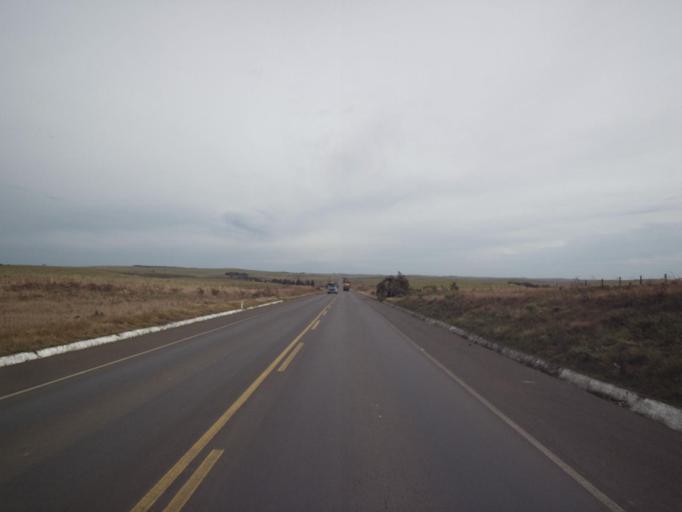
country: BR
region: Parana
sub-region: Palmas
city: Palmas
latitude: -26.7204
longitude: -51.6227
